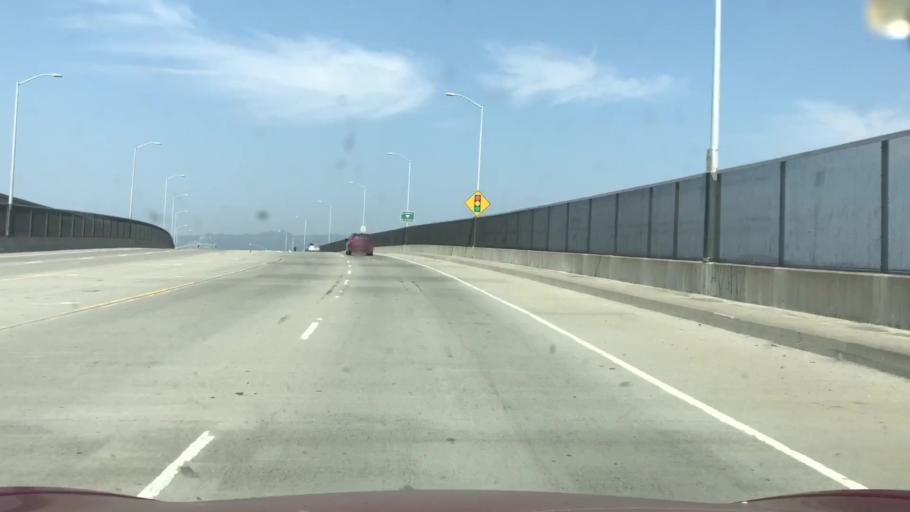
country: US
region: California
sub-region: Alameda County
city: Emeryville
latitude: 37.8173
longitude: -122.2958
